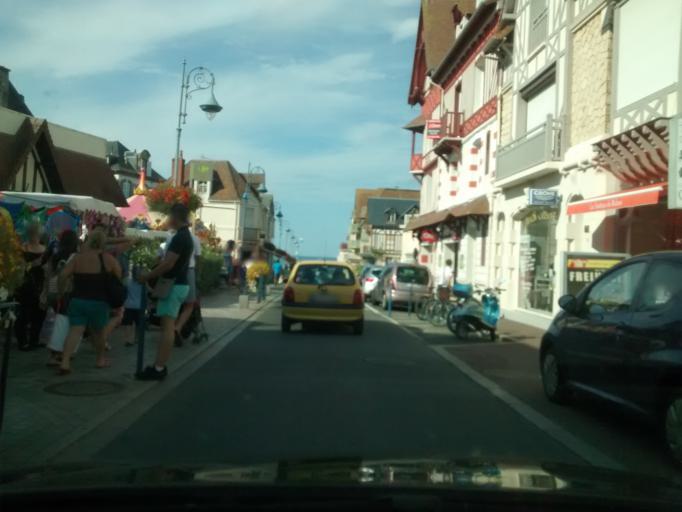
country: FR
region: Lower Normandy
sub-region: Departement du Calvados
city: Villers-sur-Mer
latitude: 49.3224
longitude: -0.0054
